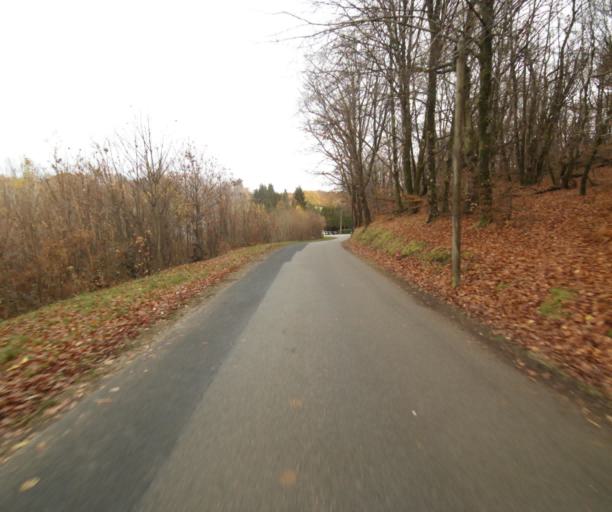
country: FR
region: Limousin
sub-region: Departement de la Correze
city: Sainte-Fortunade
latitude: 45.2178
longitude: 1.7656
